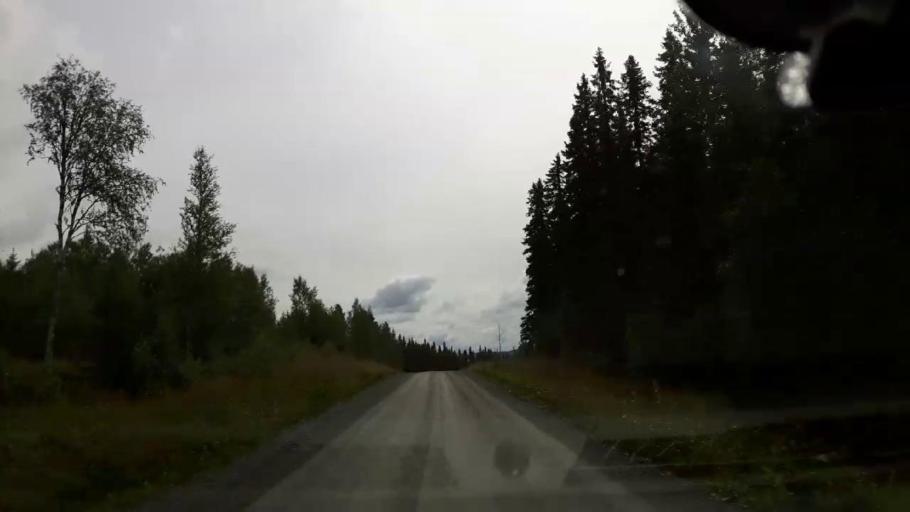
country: SE
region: Jaemtland
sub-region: Krokoms Kommun
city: Valla
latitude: 63.6468
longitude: 13.9884
